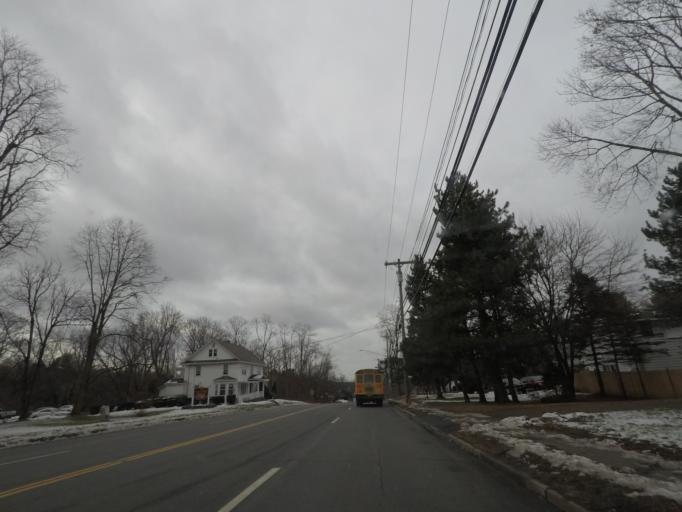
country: US
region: New York
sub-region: Rensselaer County
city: East Greenbush
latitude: 42.5911
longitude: -73.7020
